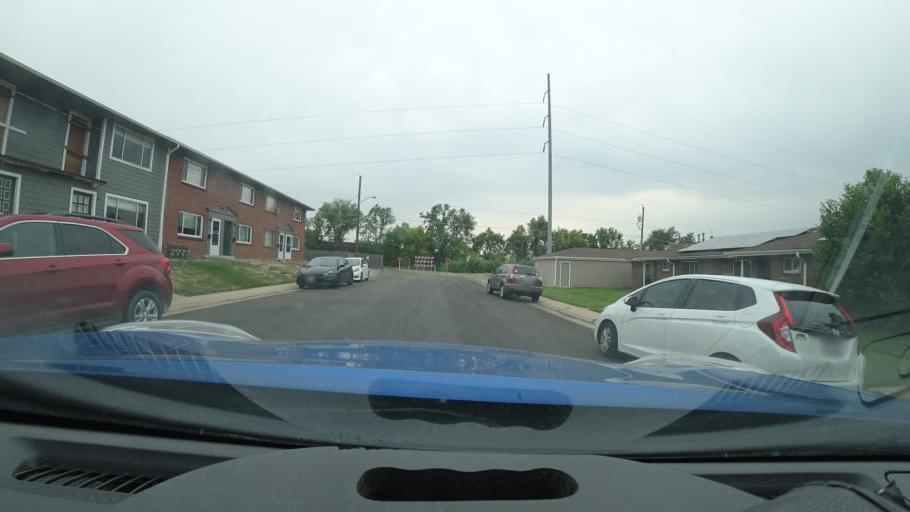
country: US
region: Colorado
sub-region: Arapahoe County
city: Glendale
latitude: 39.6802
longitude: -104.9262
